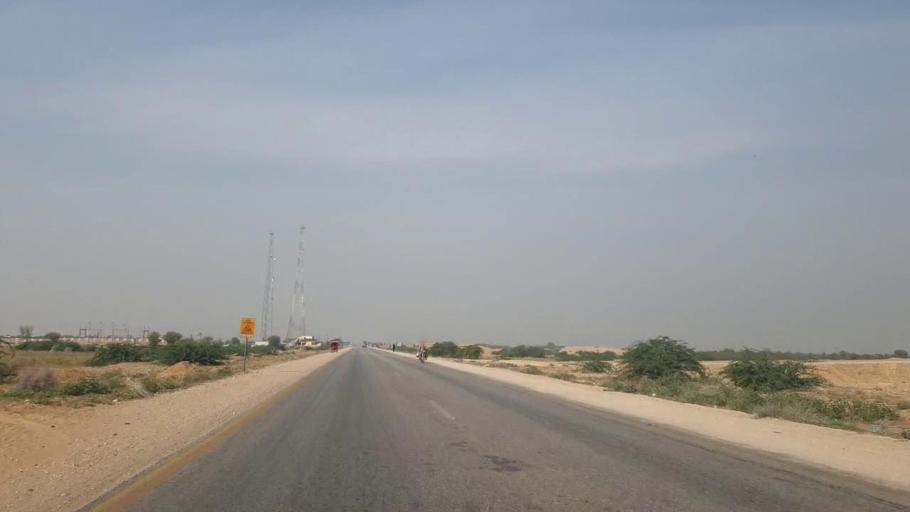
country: PK
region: Sindh
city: Sann
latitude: 26.0508
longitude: 68.1082
